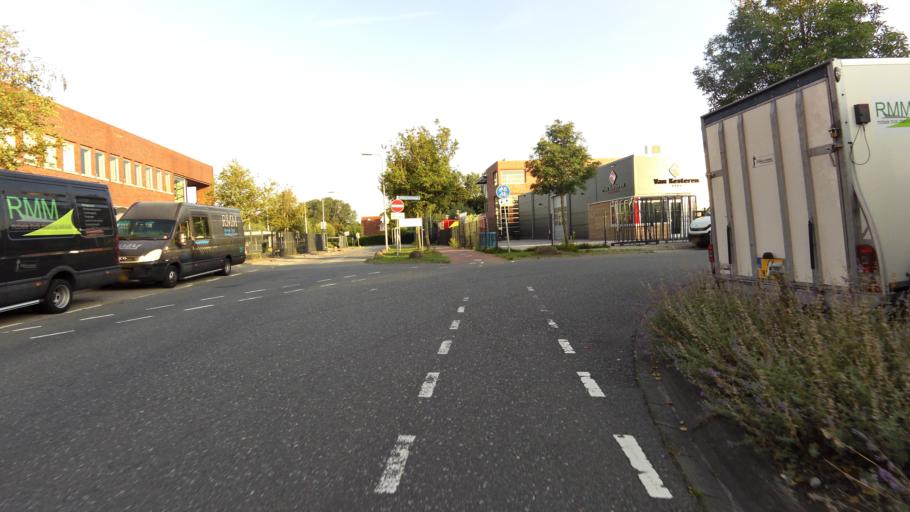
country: NL
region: South Holland
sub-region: Gemeente Teylingen
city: Voorhout
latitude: 52.2096
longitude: 4.4916
